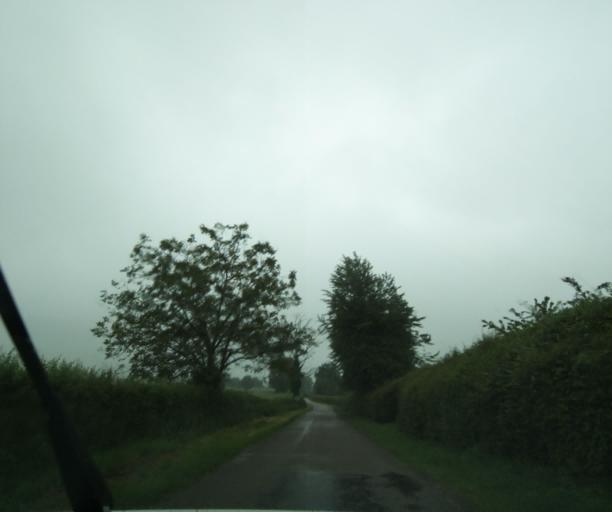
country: FR
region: Bourgogne
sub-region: Departement de Saone-et-Loire
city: Charolles
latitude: 46.4211
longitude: 4.2796
